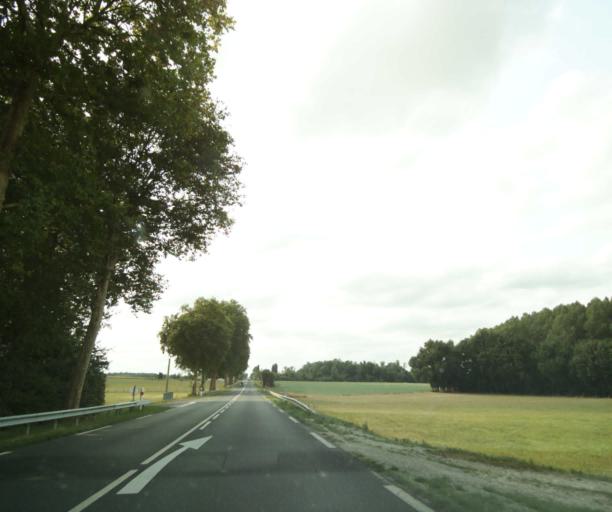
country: FR
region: Centre
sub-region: Departement de l'Indre
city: Clion
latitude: 46.9172
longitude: 1.3143
